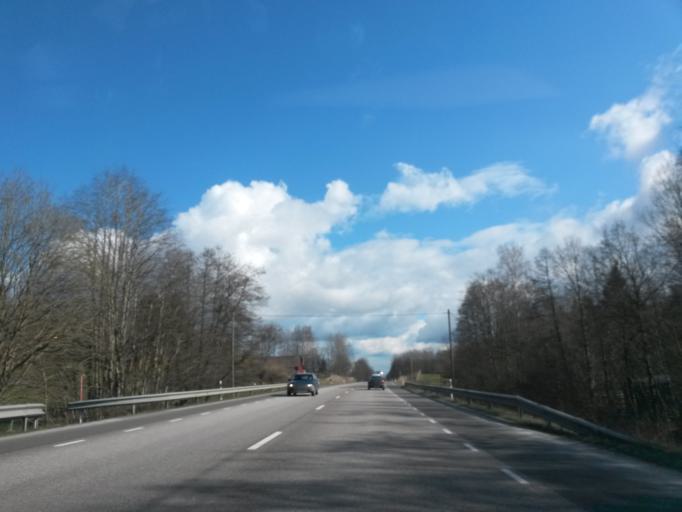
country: SE
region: Vaestra Goetaland
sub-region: Skovde Kommun
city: Skoevde
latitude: 58.3906
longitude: 13.7876
